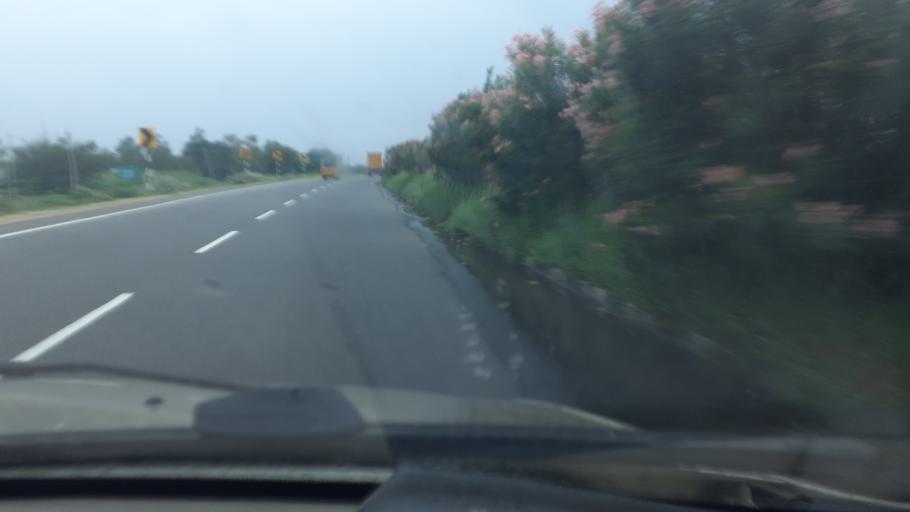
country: IN
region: Tamil Nadu
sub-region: Virudhunagar
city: Virudunagar
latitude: 9.6292
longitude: 77.9597
